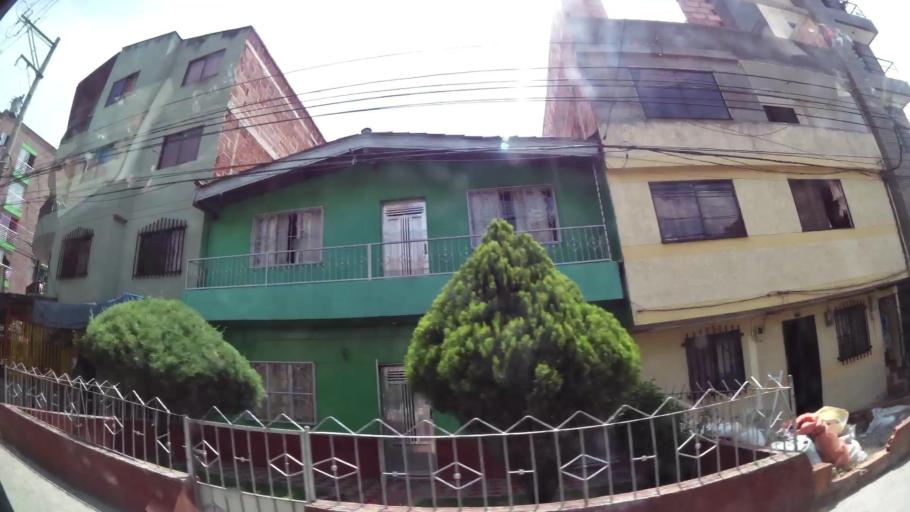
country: CO
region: Antioquia
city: Bello
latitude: 6.3404
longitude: -75.5517
